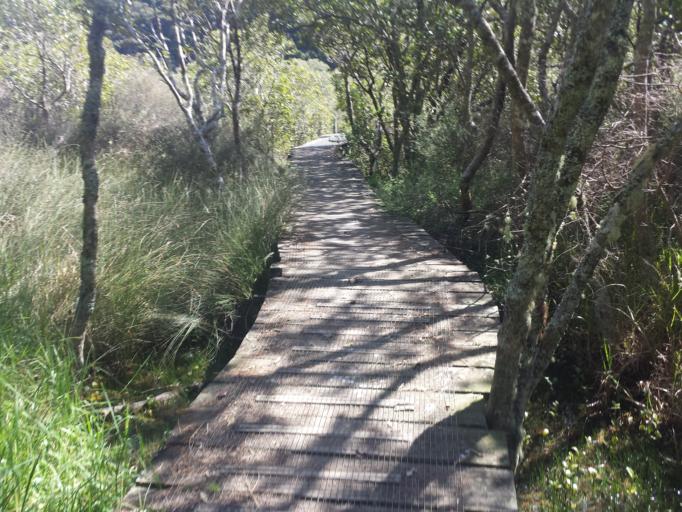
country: NZ
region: Northland
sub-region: Far North District
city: Paihia
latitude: -35.3046
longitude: 174.1026
